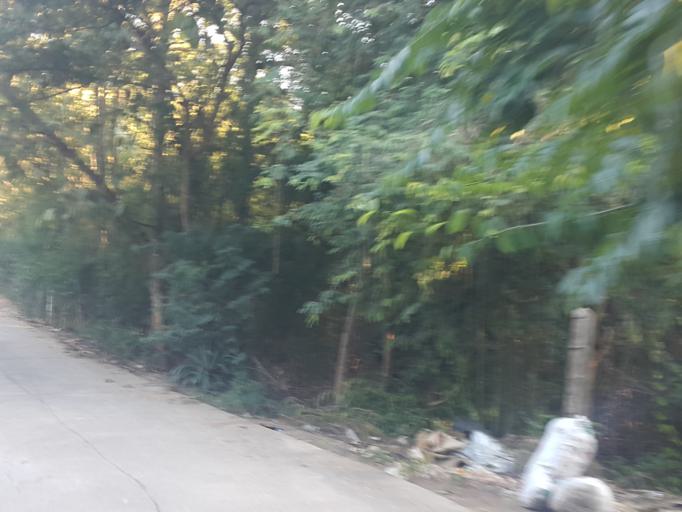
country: TH
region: Chiang Mai
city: San Sai
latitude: 18.8695
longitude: 99.1406
